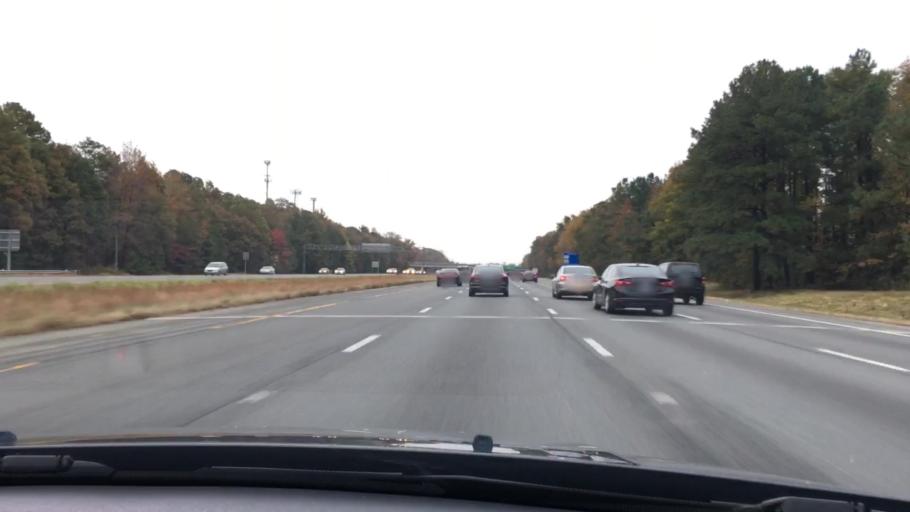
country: US
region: Virginia
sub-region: Hanover County
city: Mechanicsville
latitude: 37.6335
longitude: -77.3868
